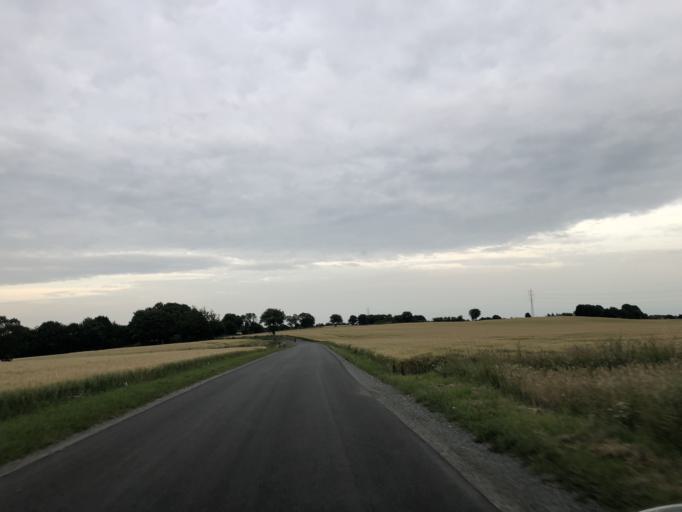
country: DK
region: South Denmark
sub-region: Vejle Kommune
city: Jelling
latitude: 55.7261
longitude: 9.4015
